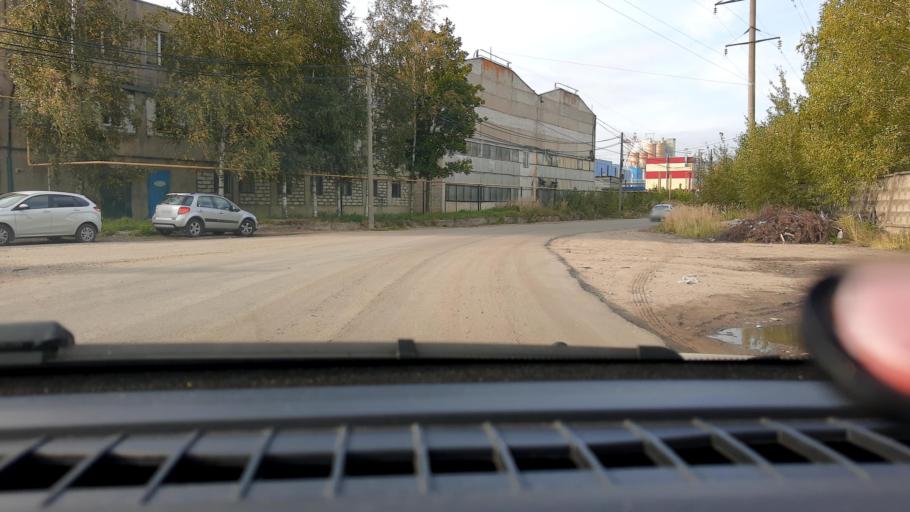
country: RU
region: Nizjnij Novgorod
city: Burevestnik
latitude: 56.1623
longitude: 43.9074
